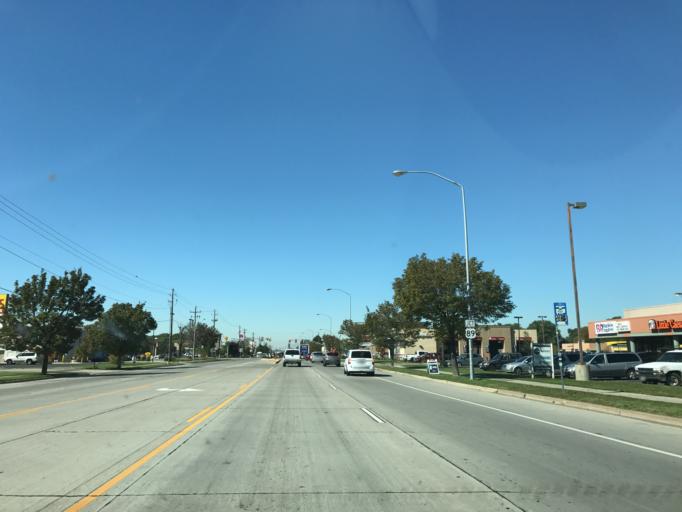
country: US
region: Utah
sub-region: Weber County
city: Ogden
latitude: 41.2443
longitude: -111.9675
